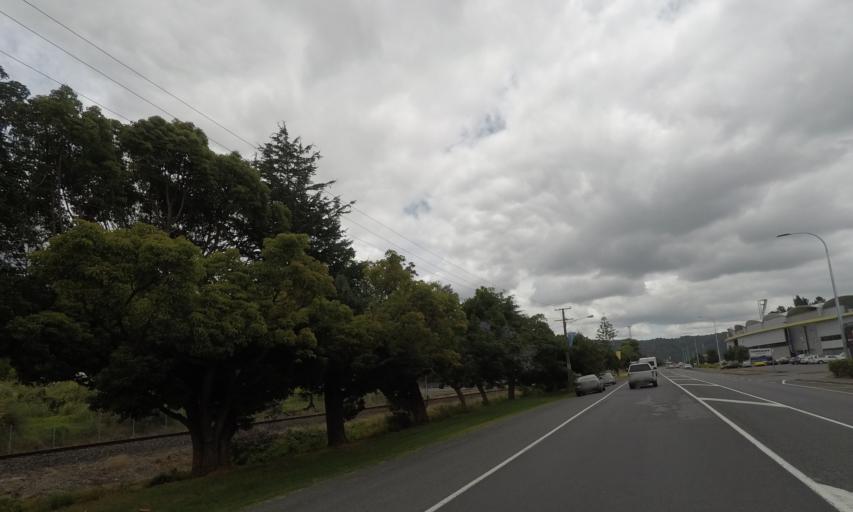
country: NZ
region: Northland
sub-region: Whangarei
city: Whangarei
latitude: -35.7359
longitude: 174.3306
